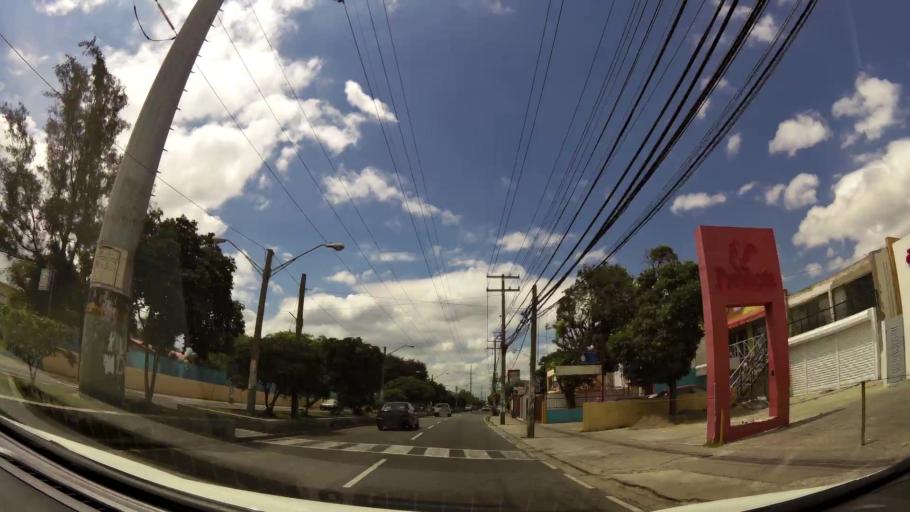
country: DO
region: Nacional
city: Bella Vista
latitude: 18.4392
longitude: -69.9488
